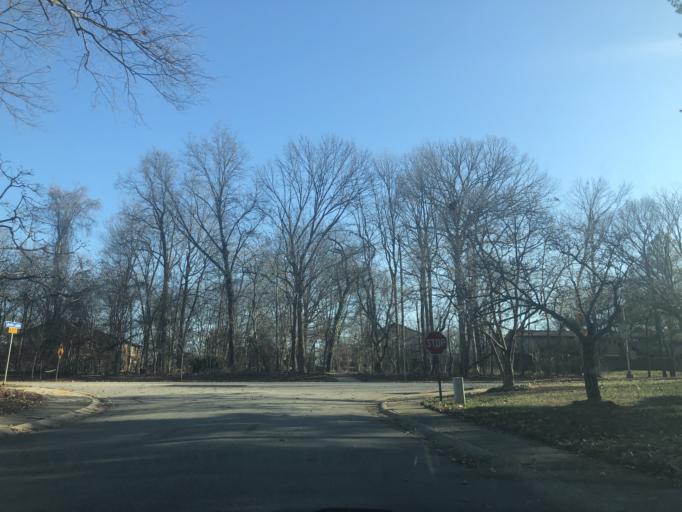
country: US
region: Maryland
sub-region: Howard County
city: Columbia
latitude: 39.2067
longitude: -76.8481
